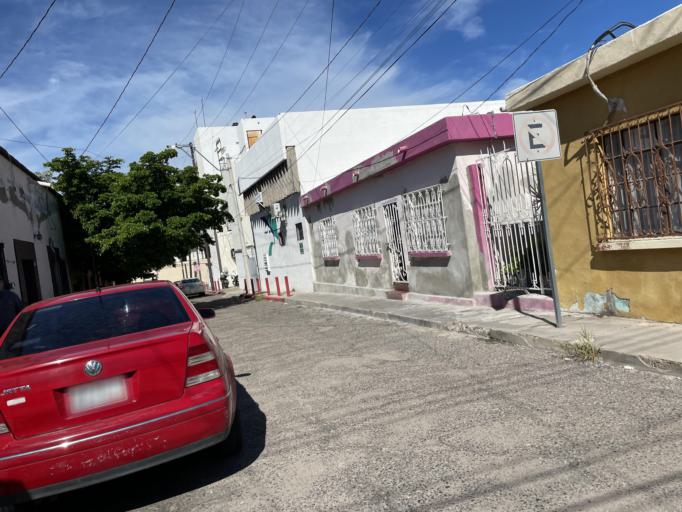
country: MX
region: Sonora
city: Hermosillo
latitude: 29.0745
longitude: -110.9555
